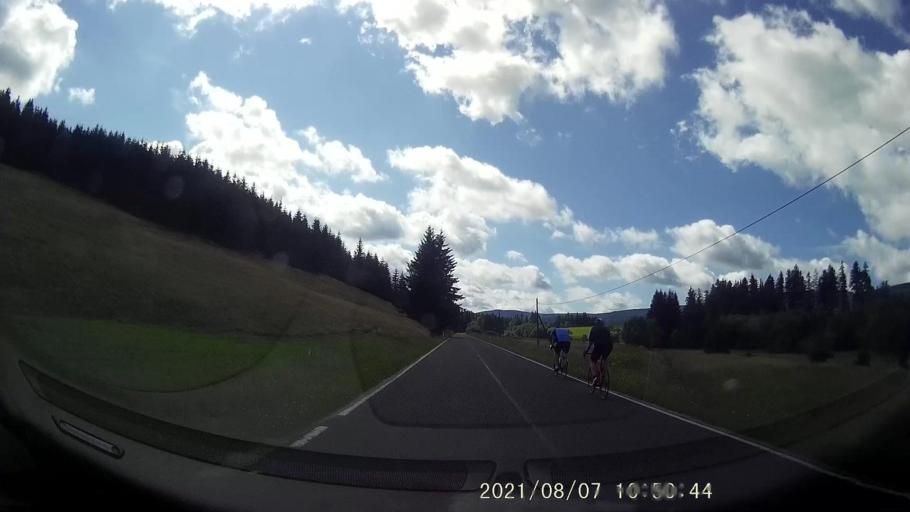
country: PL
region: Lower Silesian Voivodeship
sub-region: Powiat klodzki
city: Polanica-Zdroj
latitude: 50.2952
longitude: 16.4659
